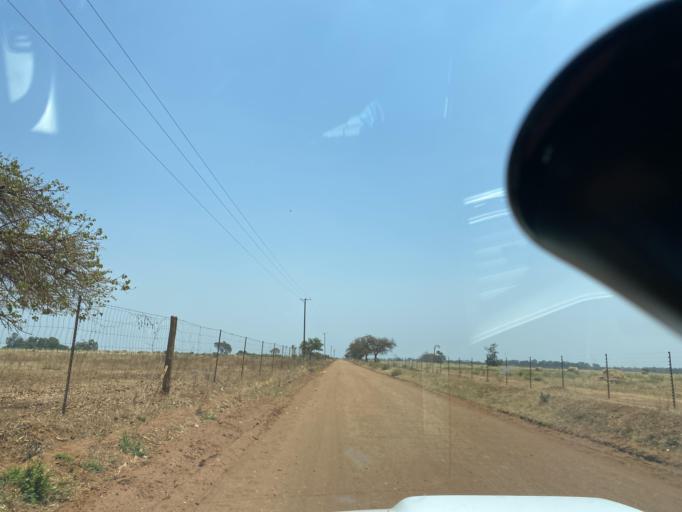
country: ZM
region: Lusaka
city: Lusaka
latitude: -15.4409
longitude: 28.0559
